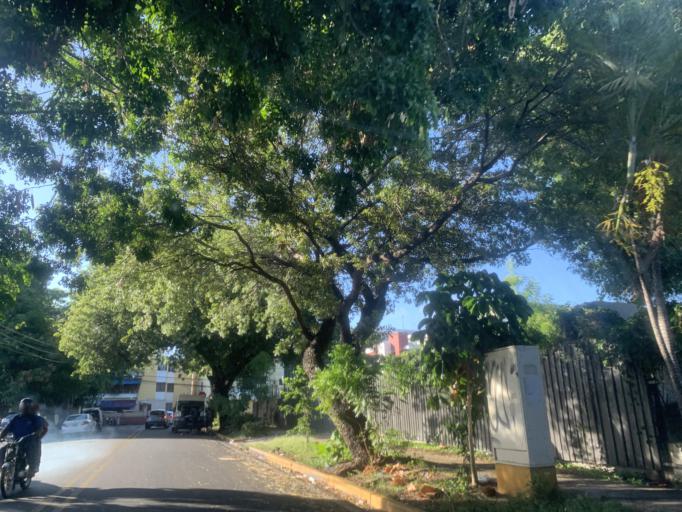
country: DO
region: Nacional
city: Ciudad Nueva
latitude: 18.4618
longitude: -69.9041
